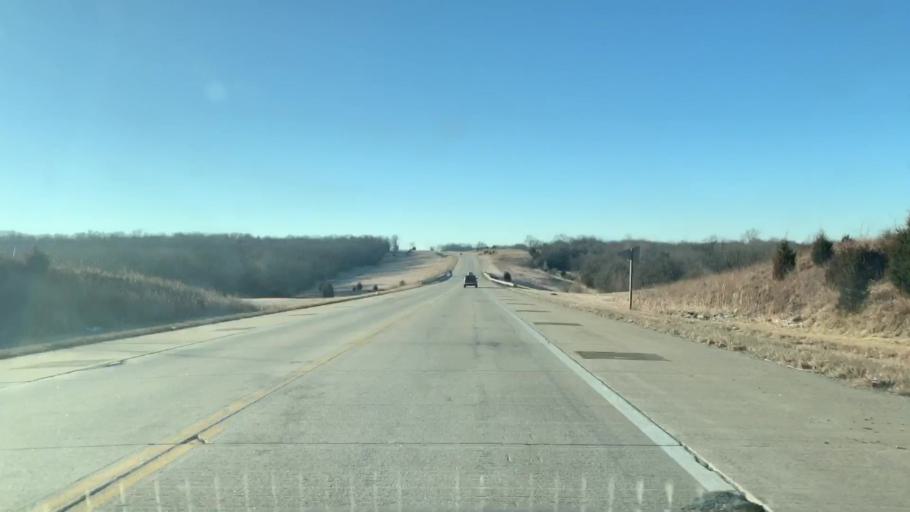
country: US
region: Kansas
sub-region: Crawford County
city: Arma
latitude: 37.5862
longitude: -94.7055
